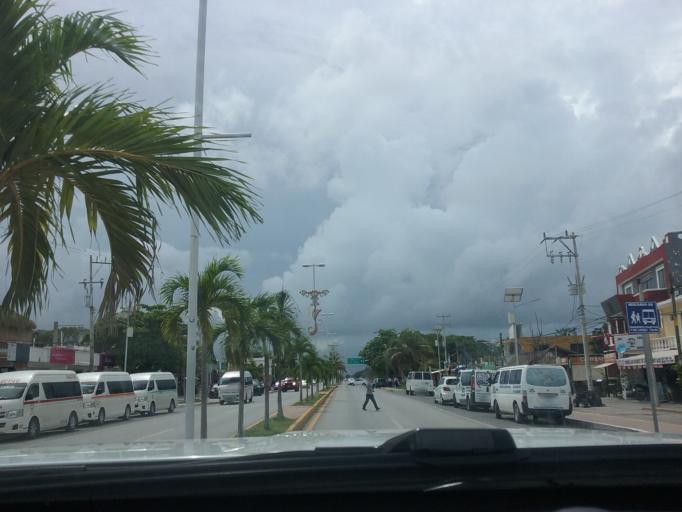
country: MX
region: Quintana Roo
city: Tulum
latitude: 20.2103
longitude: -87.4657
